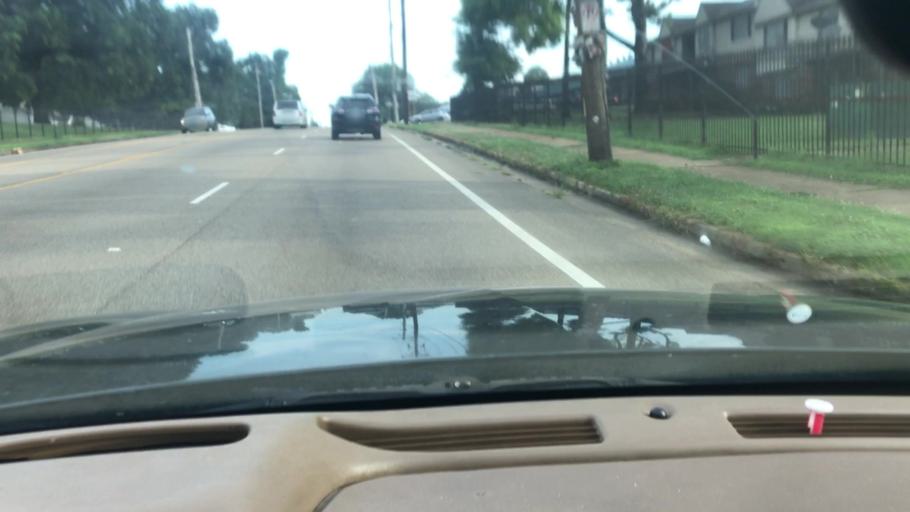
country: US
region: Tennessee
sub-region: Shelby County
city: New South Memphis
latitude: 35.0503
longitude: -90.0076
